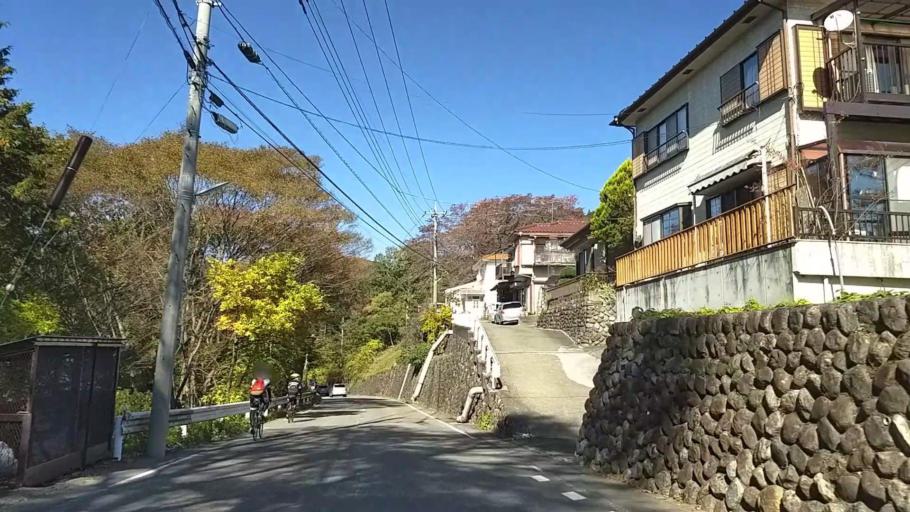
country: JP
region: Yamanashi
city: Uenohara
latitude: 35.6404
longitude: 139.1027
